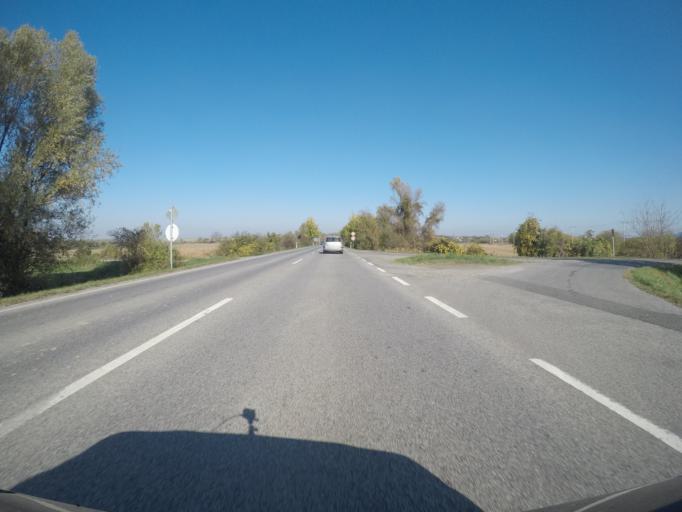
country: HU
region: Baranya
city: Hidas
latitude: 46.2654
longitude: 18.5116
